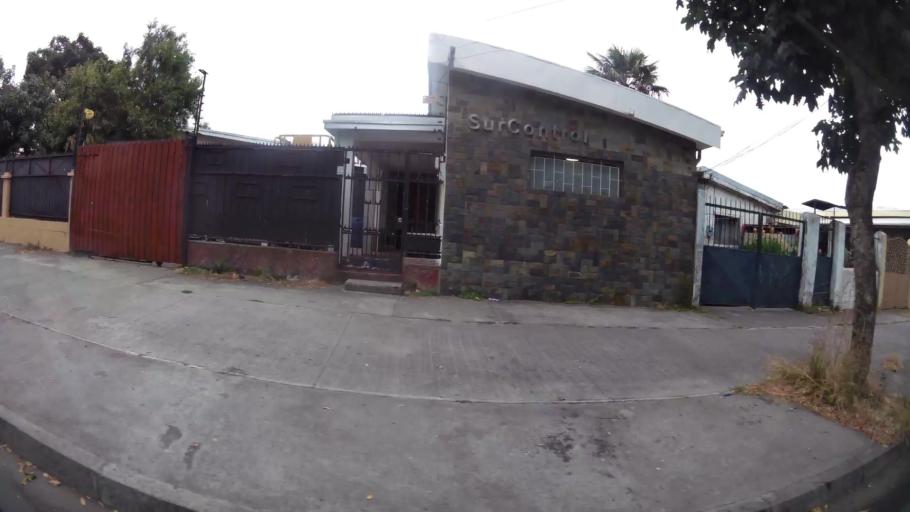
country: CL
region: Biobio
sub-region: Provincia de Concepcion
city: Concepcion
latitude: -36.8214
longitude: -73.0628
